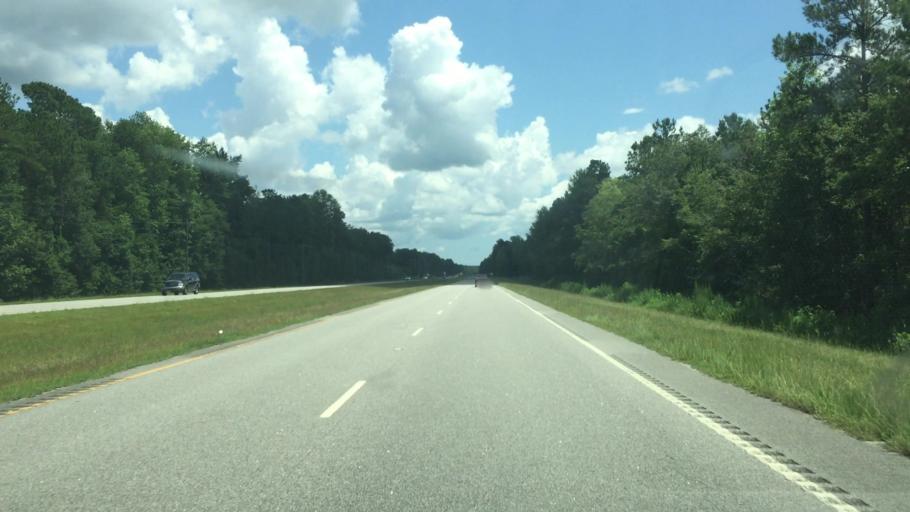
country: US
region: South Carolina
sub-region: Horry County
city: Loris
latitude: 34.0430
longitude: -78.8256
